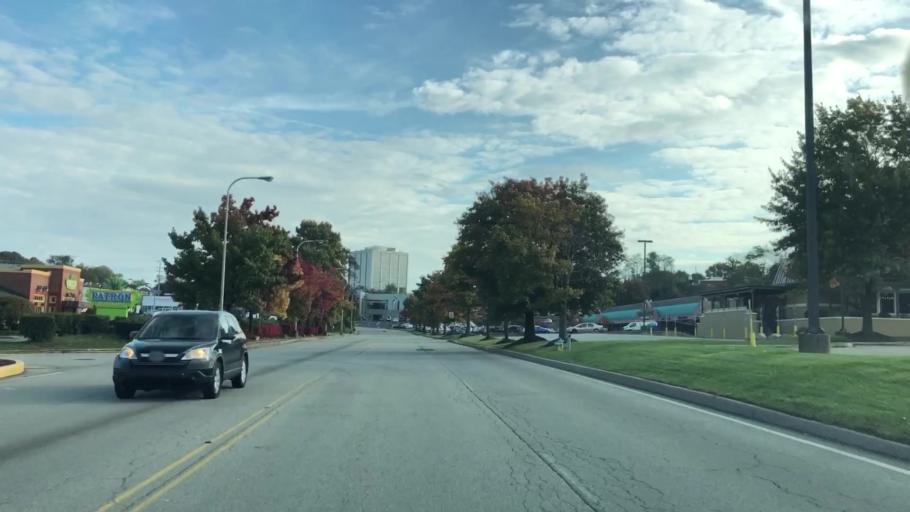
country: US
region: Pennsylvania
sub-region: Allegheny County
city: Monroeville
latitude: 40.4342
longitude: -79.7879
